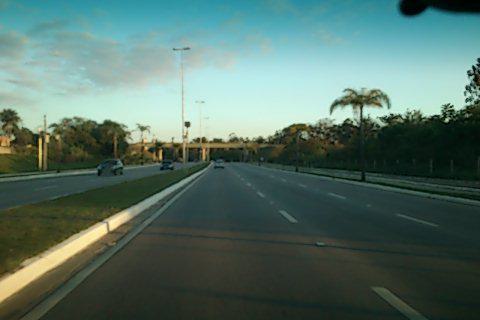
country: BR
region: Sao Paulo
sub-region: Sao Jose Dos Campos
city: Sao Jose dos Campos
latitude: -23.1727
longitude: -45.8951
